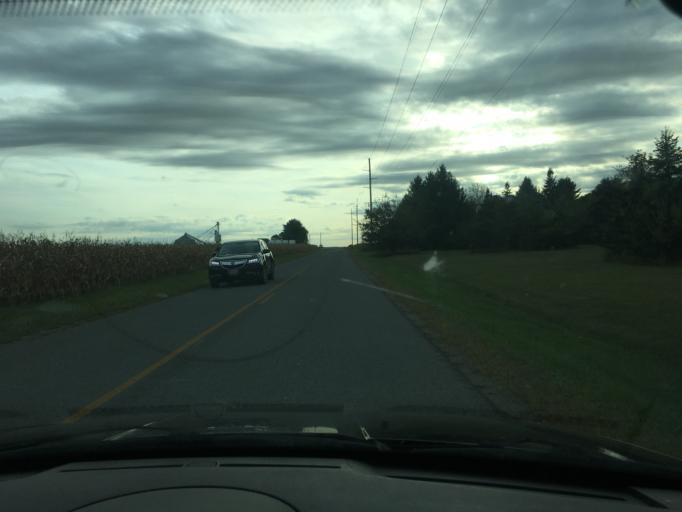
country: US
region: Ohio
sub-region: Logan County
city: West Liberty
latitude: 40.2749
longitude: -83.7094
